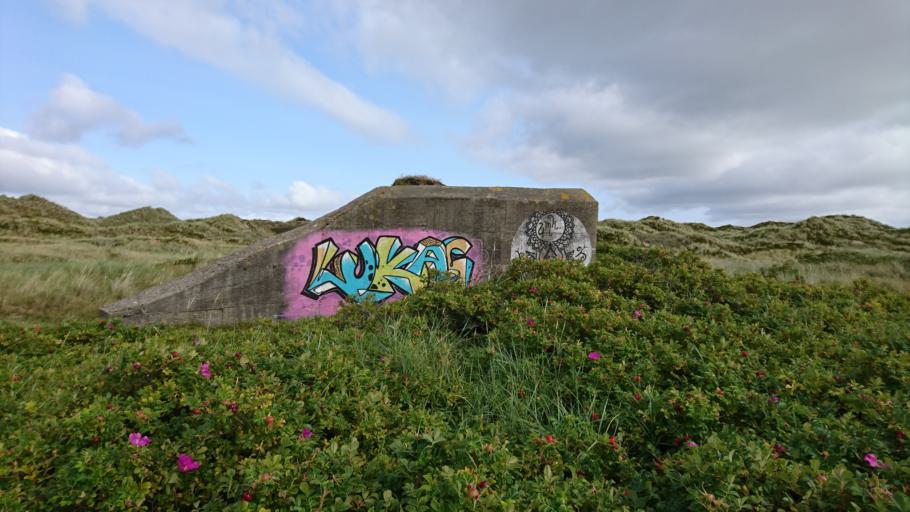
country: DK
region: South Denmark
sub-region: Fano Kommune
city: Nordby
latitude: 55.4502
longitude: 8.3549
